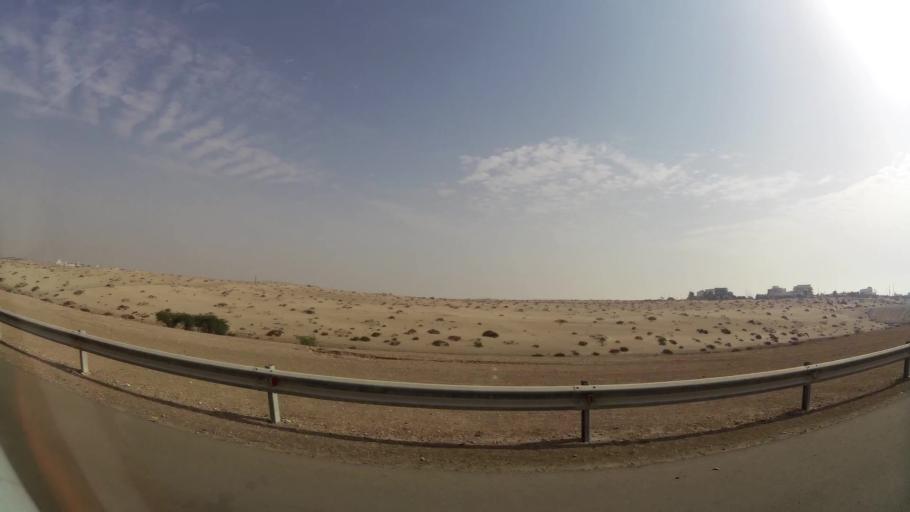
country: AE
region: Abu Dhabi
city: Abu Dhabi
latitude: 24.2669
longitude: 54.6851
